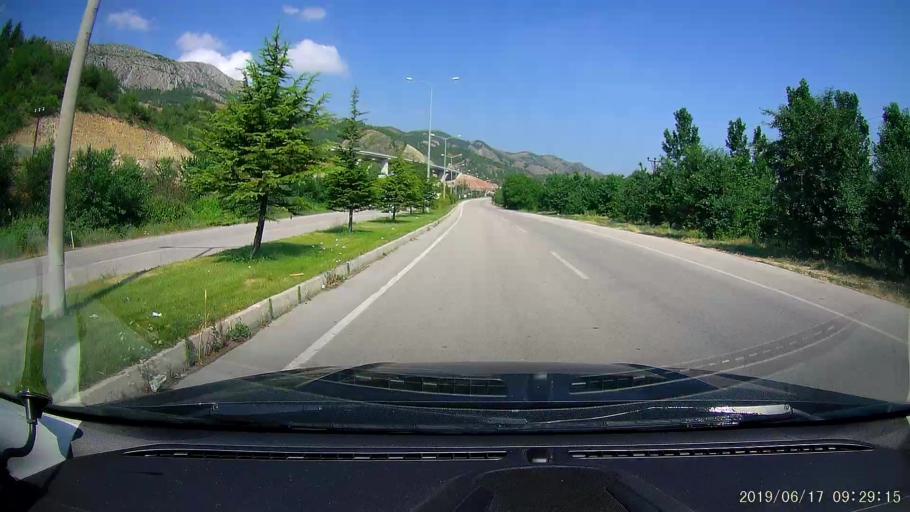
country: TR
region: Amasya
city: Amasya
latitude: 40.6953
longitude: 35.8145
